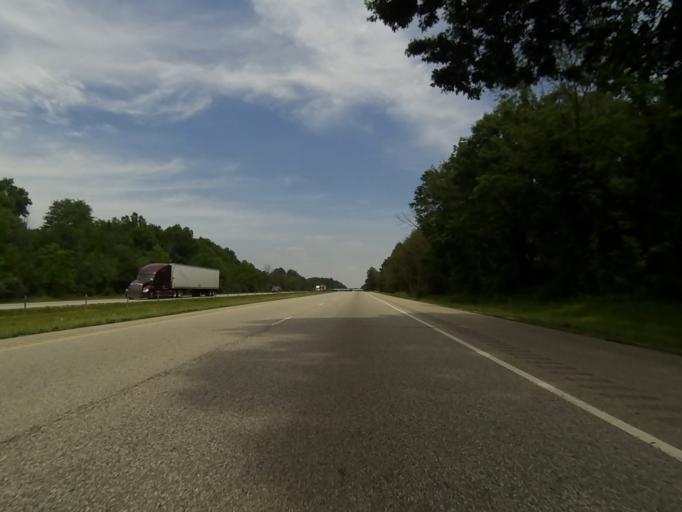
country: US
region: Ohio
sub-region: Mahoning County
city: Craig Beach
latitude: 41.0998
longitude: -81.0112
